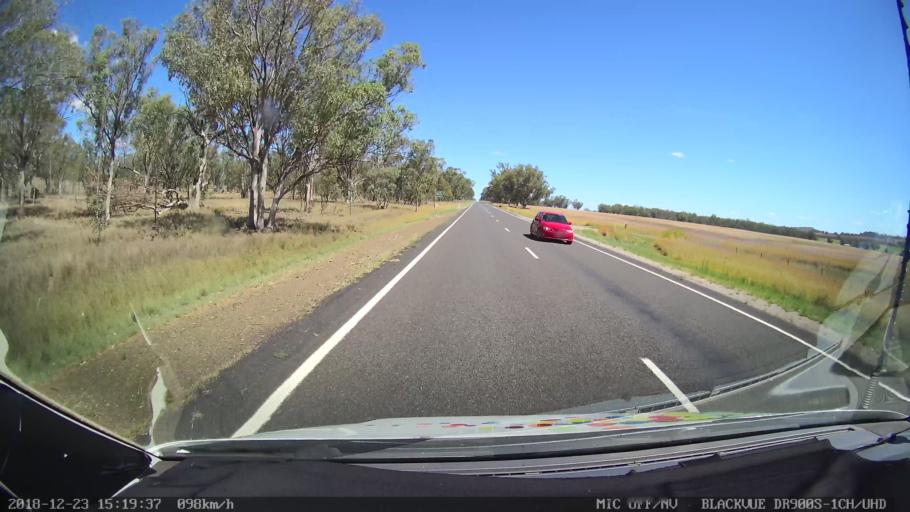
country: AU
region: New South Wales
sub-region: Tamworth Municipality
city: Manilla
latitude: -30.8313
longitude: 150.7840
